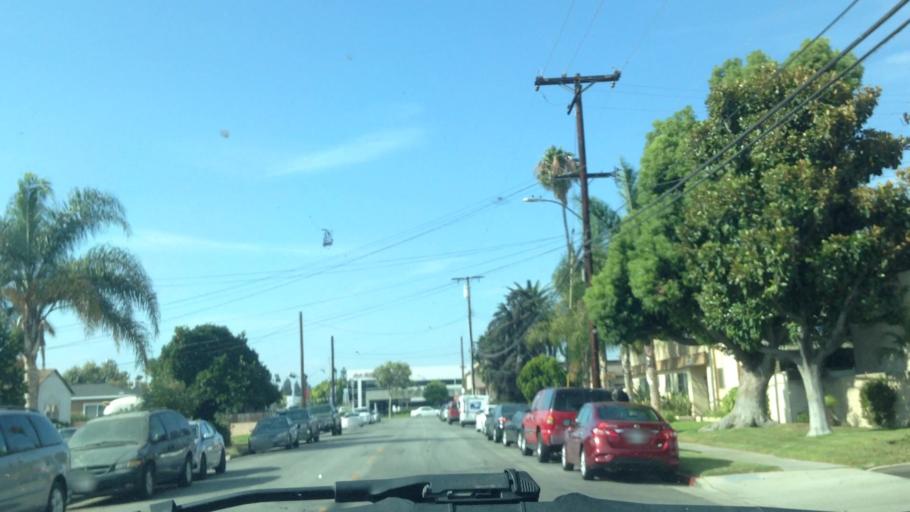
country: US
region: California
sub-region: Orange County
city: Garden Grove
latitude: 33.7727
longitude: -117.9485
